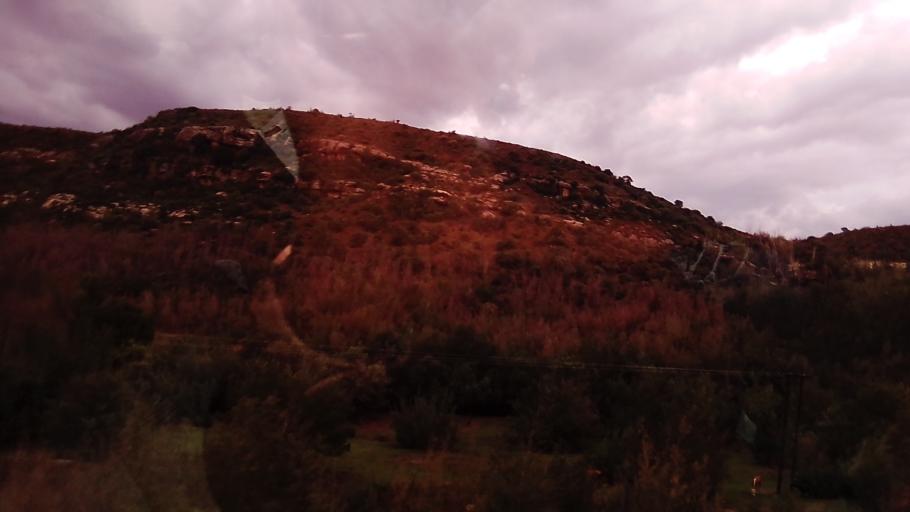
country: LS
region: Berea
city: Teyateyaneng
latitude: -29.3307
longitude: 27.7036
